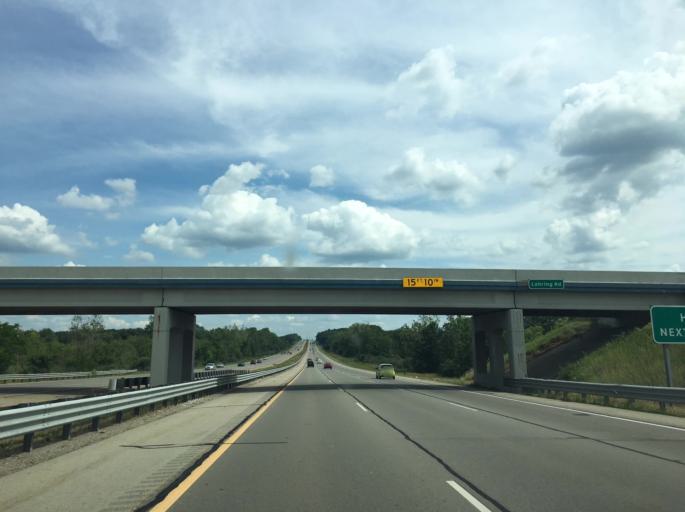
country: US
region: Michigan
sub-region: Oakland County
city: Holly
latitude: 42.8443
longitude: -83.5854
